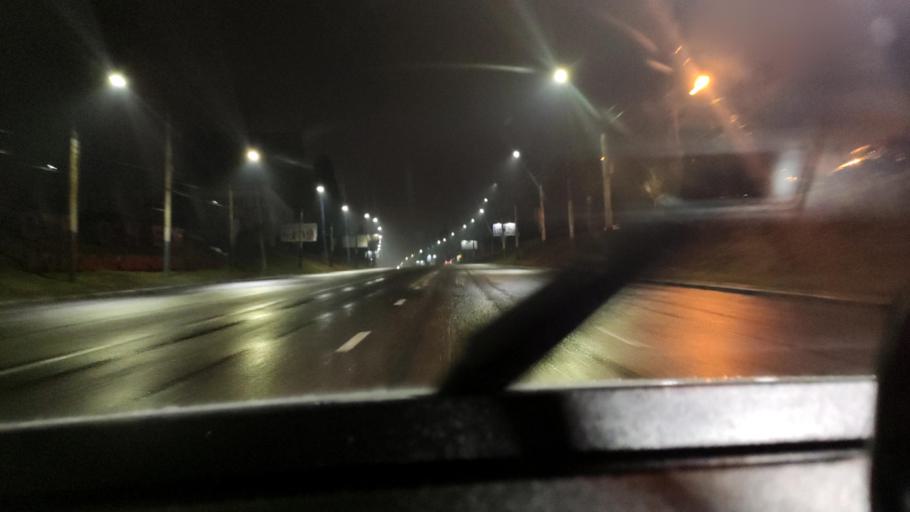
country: RU
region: Voronezj
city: Voronezh
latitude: 51.6415
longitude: 39.2036
